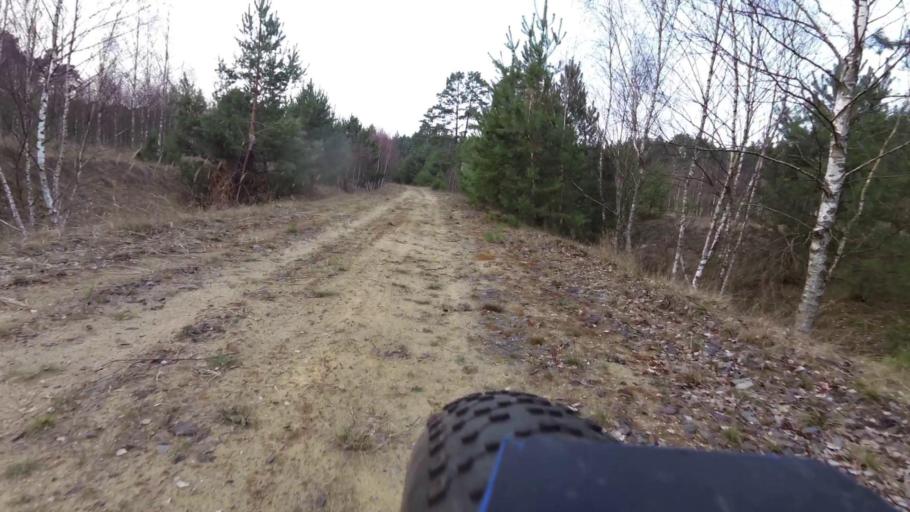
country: PL
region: Lubusz
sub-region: Powiat slubicki
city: Cybinka
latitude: 52.2408
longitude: 14.7720
